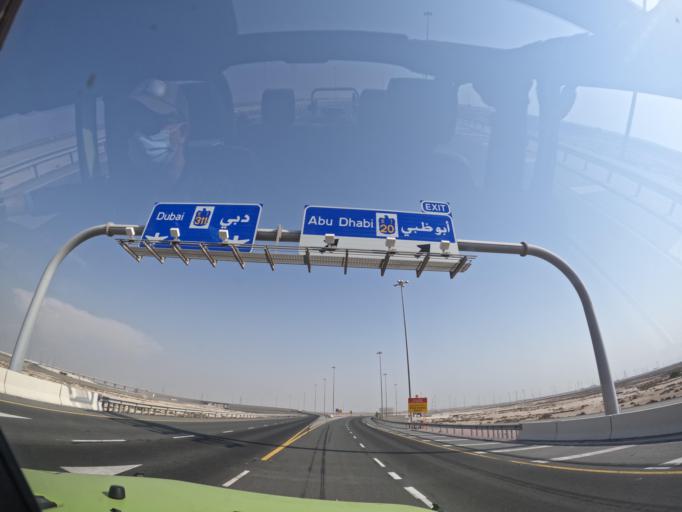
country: AE
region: Abu Dhabi
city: Abu Dhabi
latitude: 24.6801
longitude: 54.8098
